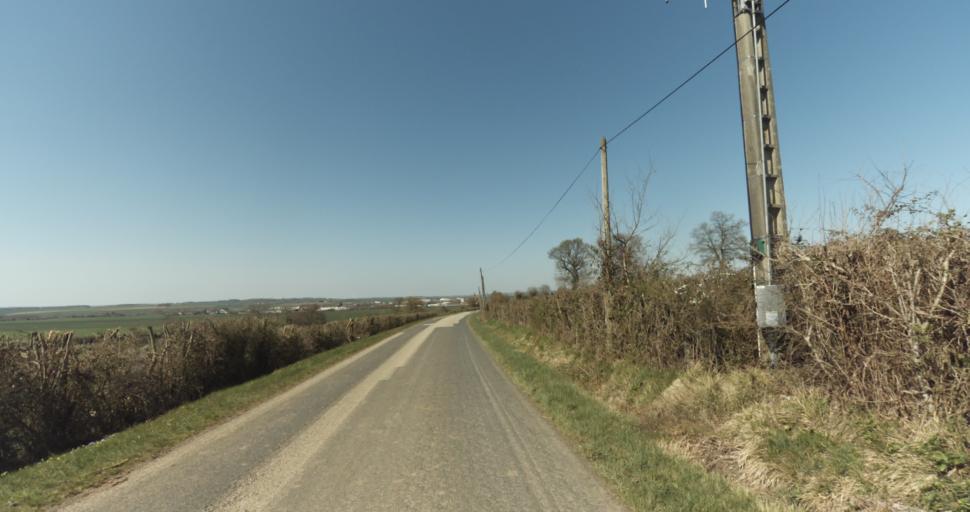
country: FR
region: Lower Normandy
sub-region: Departement du Calvados
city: Saint-Pierre-sur-Dives
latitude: 49.0080
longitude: -0.0157
